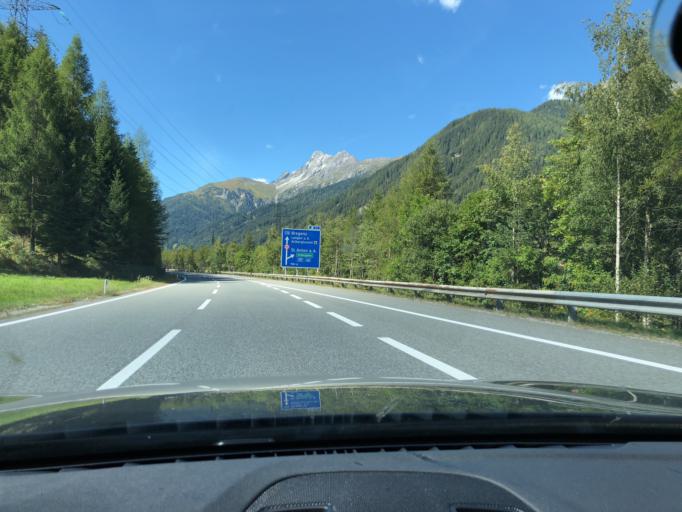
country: AT
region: Tyrol
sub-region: Politischer Bezirk Landeck
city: Flirsch
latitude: 47.1436
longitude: 10.3325
